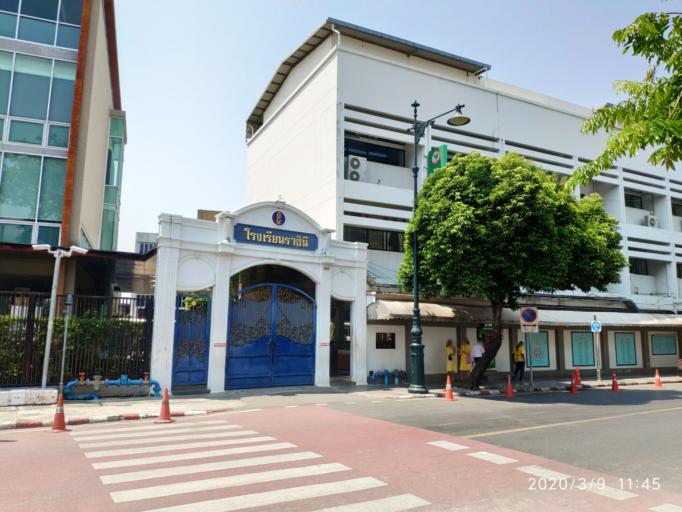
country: TH
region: Bangkok
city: Bangkok
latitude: 13.7430
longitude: 100.4944
